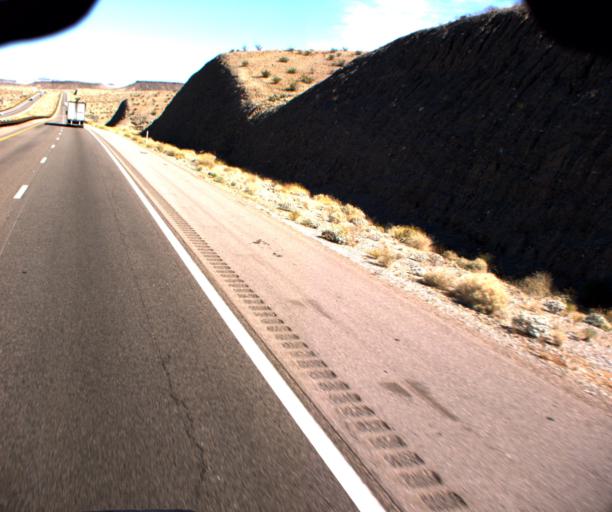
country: US
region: Nevada
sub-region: Clark County
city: Boulder City
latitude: 35.9164
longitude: -114.6297
